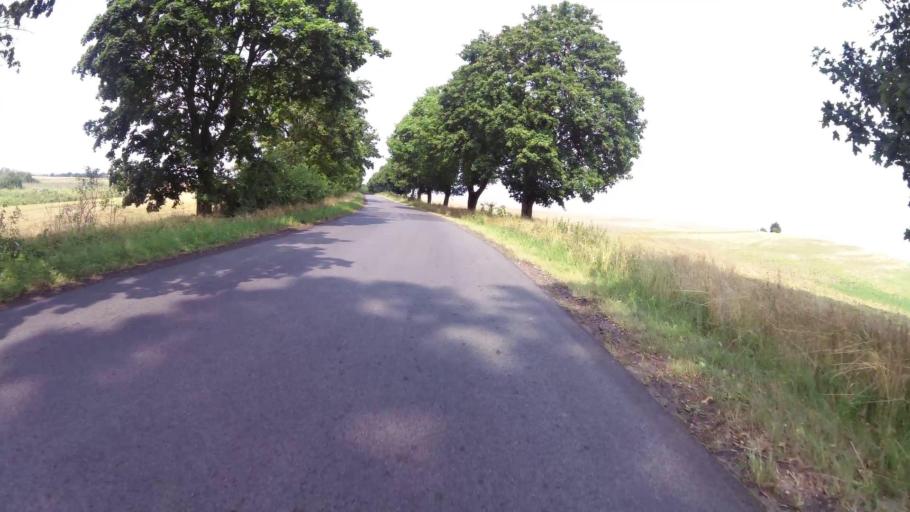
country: PL
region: West Pomeranian Voivodeship
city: Trzcinsko Zdroj
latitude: 52.9429
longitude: 14.6439
